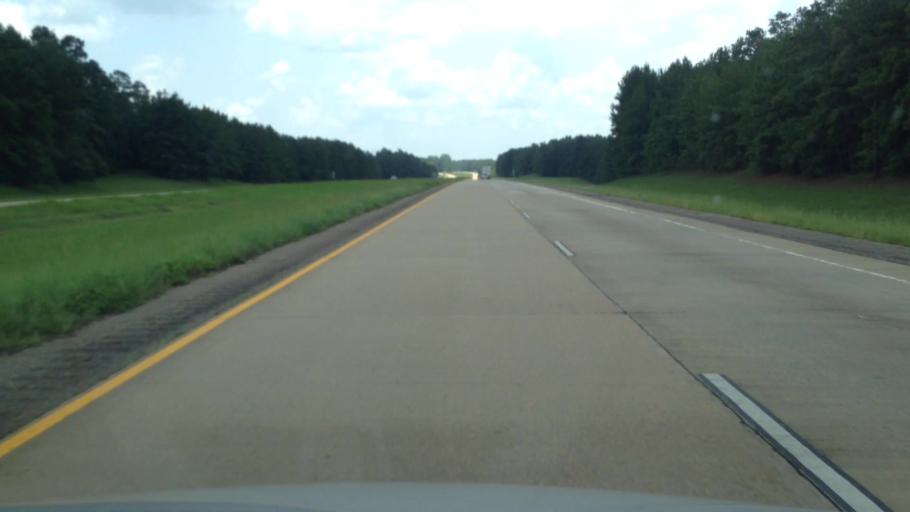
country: US
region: Louisiana
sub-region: Rapides Parish
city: Lecompte
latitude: 31.0499
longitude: -92.4215
